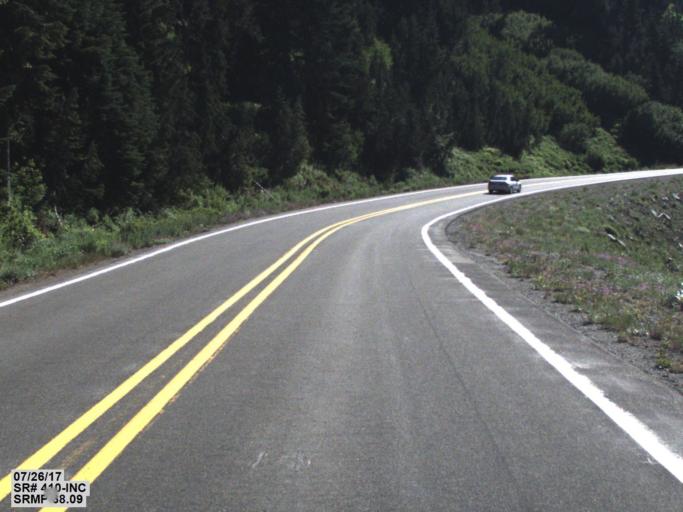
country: US
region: Washington
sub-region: King County
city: Enumclaw
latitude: 46.8711
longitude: -121.5296
